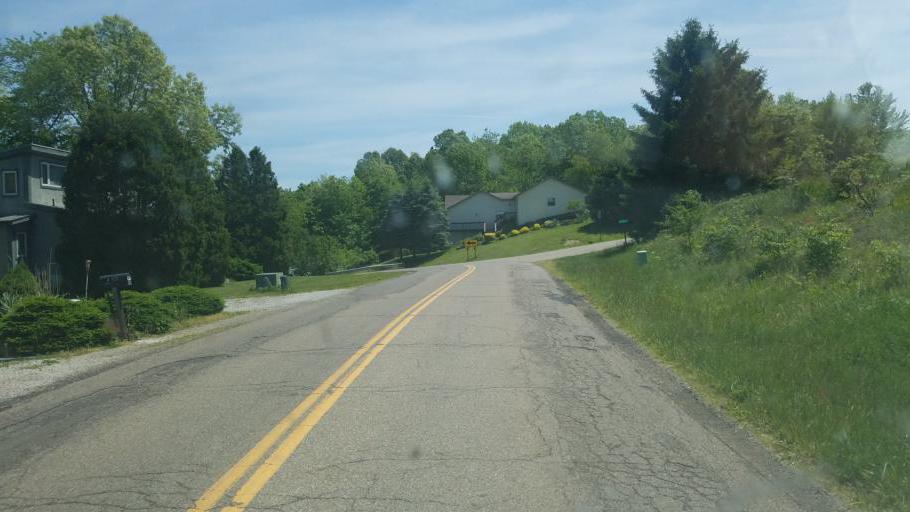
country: US
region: Ohio
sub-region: Knox County
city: Gambier
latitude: 40.4183
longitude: -82.3432
